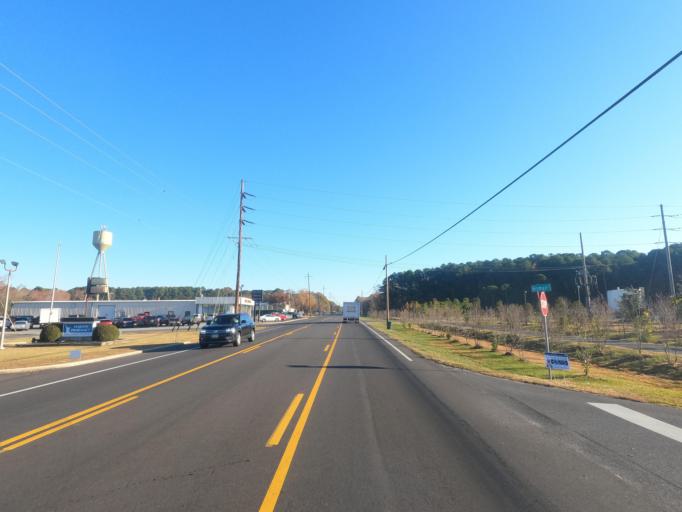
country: US
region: Maryland
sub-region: Somerset County
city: Crisfield
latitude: 37.9944
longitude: -75.8390
